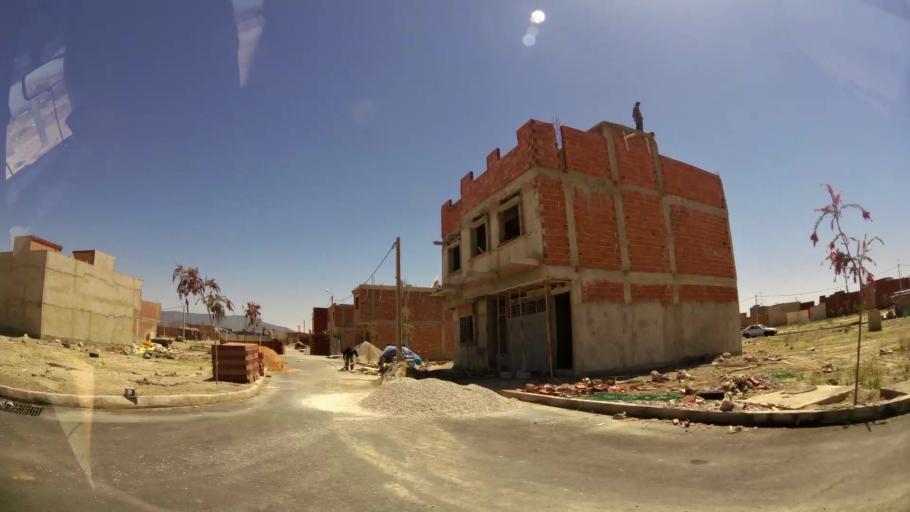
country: MA
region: Oriental
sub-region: Oujda-Angad
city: Oujda
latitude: 34.6866
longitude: -1.8633
